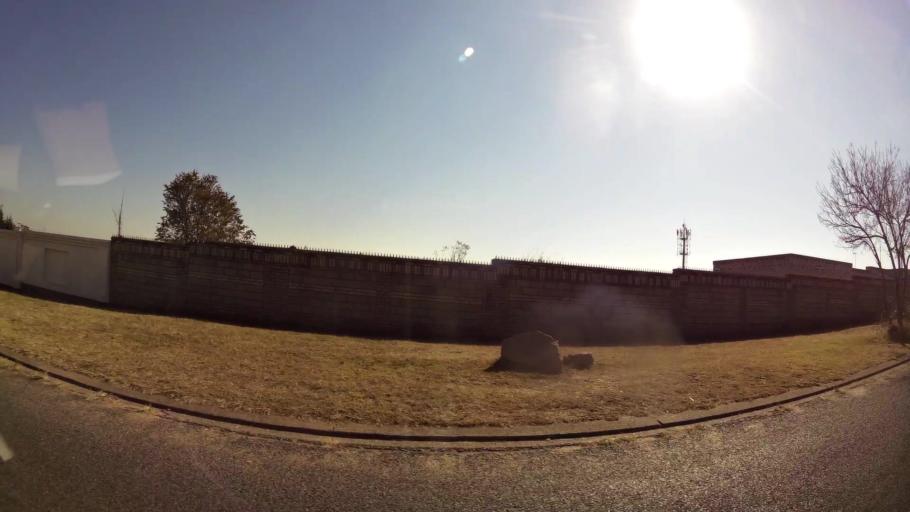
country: ZA
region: Gauteng
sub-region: City of Johannesburg Metropolitan Municipality
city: Modderfontein
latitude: -26.1126
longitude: 28.1213
